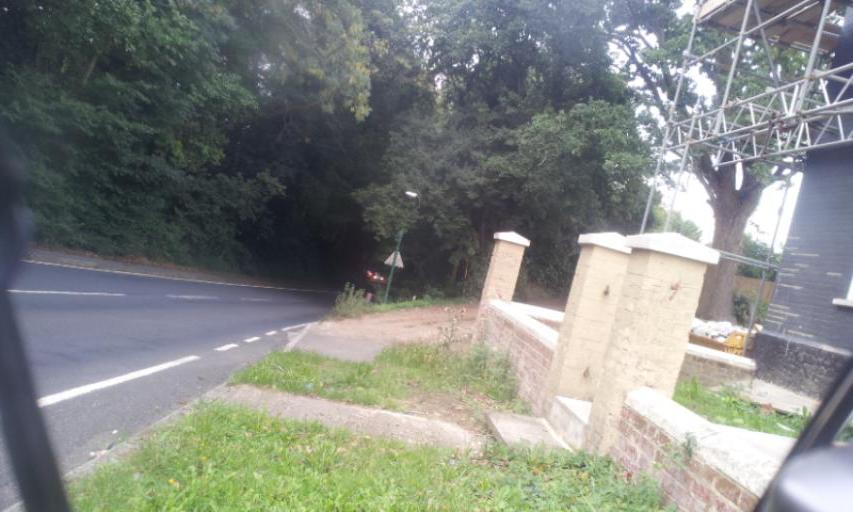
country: GB
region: England
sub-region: Kent
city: Larkfield
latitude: 51.2770
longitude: 0.4351
